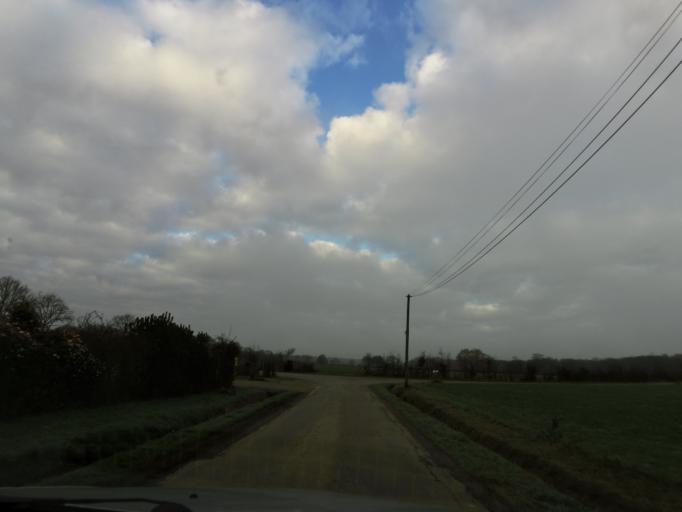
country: FR
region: Brittany
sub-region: Departement d'Ille-et-Vilaine
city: Chanteloup
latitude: 47.9435
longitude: -1.6341
